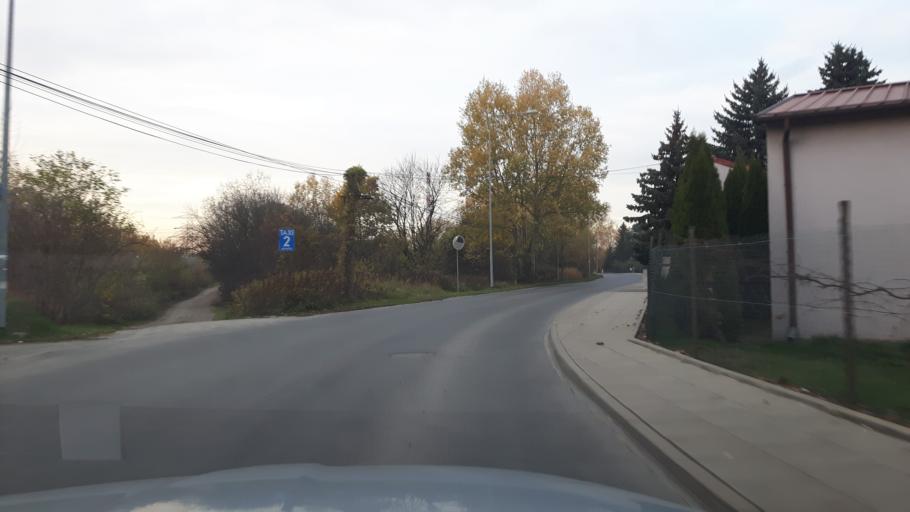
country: PL
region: Masovian Voivodeship
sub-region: Warszawa
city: Wilanow
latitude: 52.1775
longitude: 21.1042
